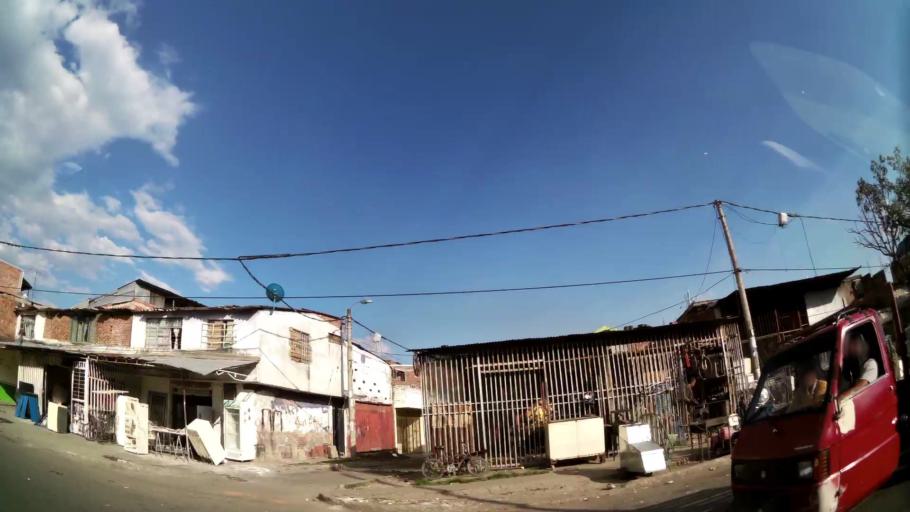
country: CO
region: Valle del Cauca
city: Cali
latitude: 3.4236
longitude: -76.4853
